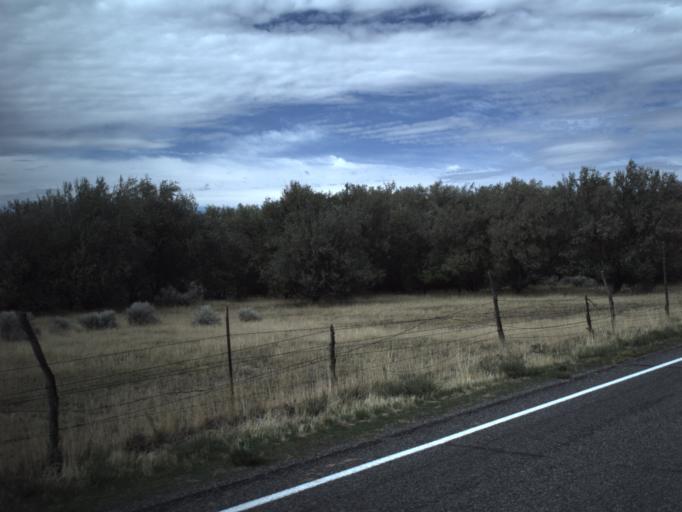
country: US
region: Utah
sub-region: Millard County
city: Fillmore
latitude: 39.0866
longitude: -112.4099
